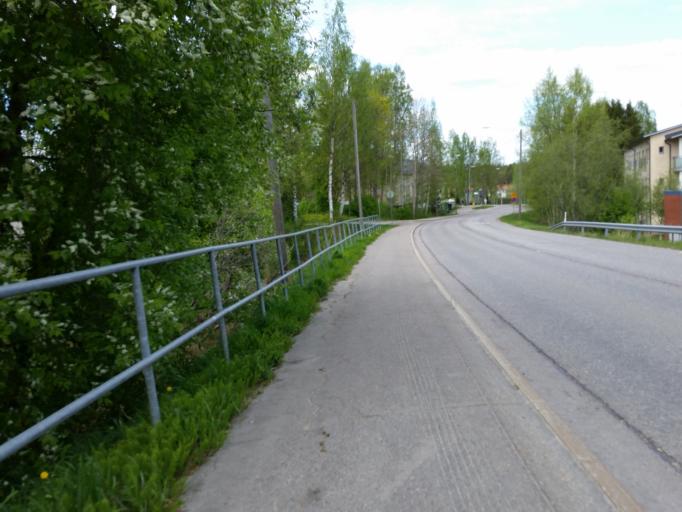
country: FI
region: Uusimaa
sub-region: Helsinki
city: Espoo
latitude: 60.2105
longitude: 24.6418
